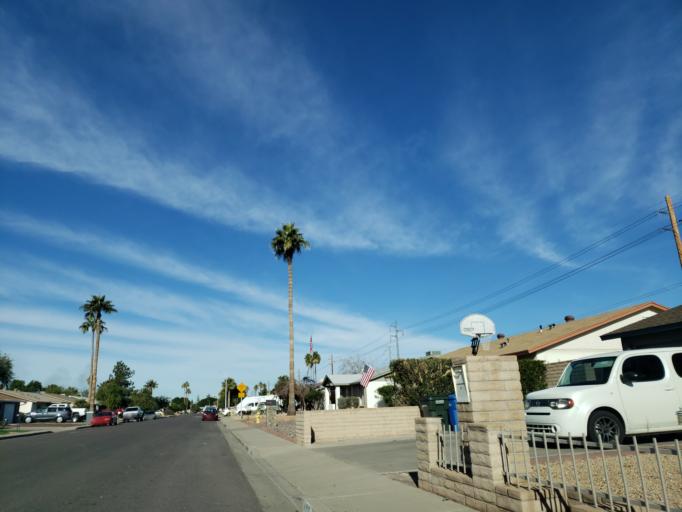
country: US
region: Arizona
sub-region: Maricopa County
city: Glendale
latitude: 33.5788
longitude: -112.1475
